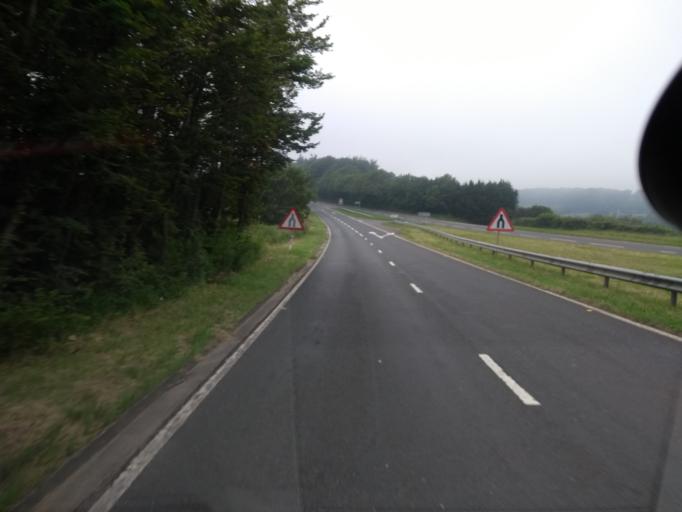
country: GB
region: England
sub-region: Dorset
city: Lyme Regis
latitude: 50.7563
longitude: -2.9387
